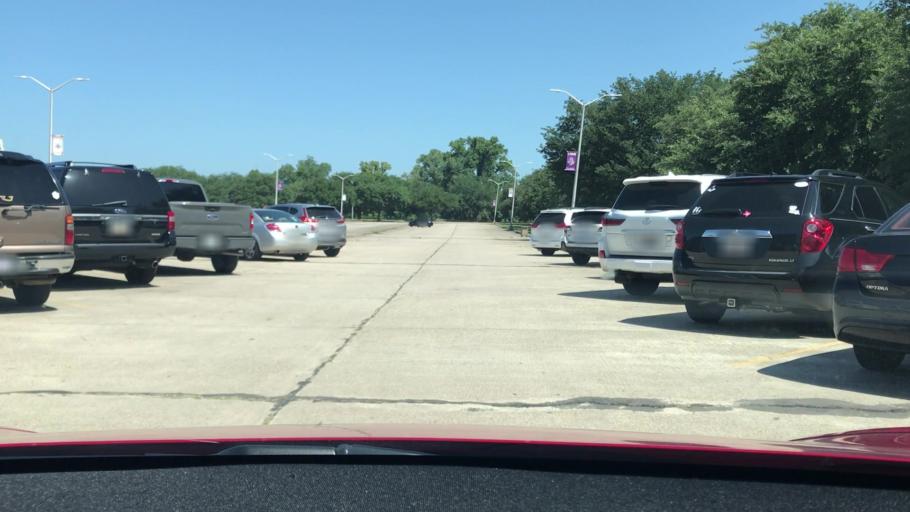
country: US
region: Louisiana
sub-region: Bossier Parish
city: Bossier City
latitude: 32.4297
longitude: -93.7045
